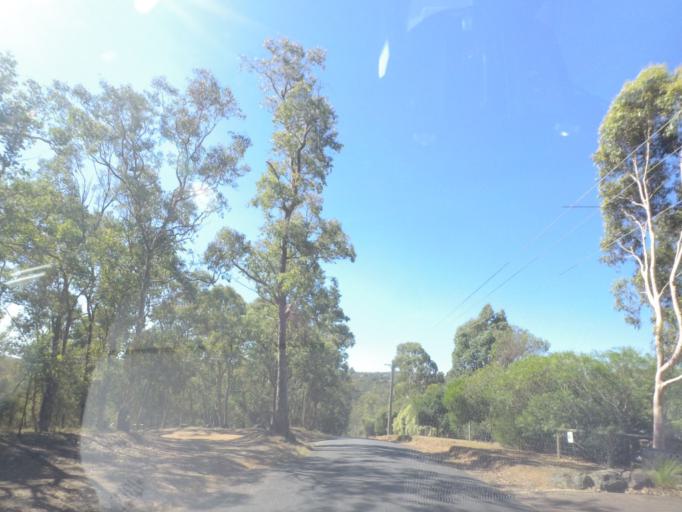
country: AU
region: Victoria
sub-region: Yarra Ranges
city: Chirnside Park
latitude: -37.7208
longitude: 145.2855
